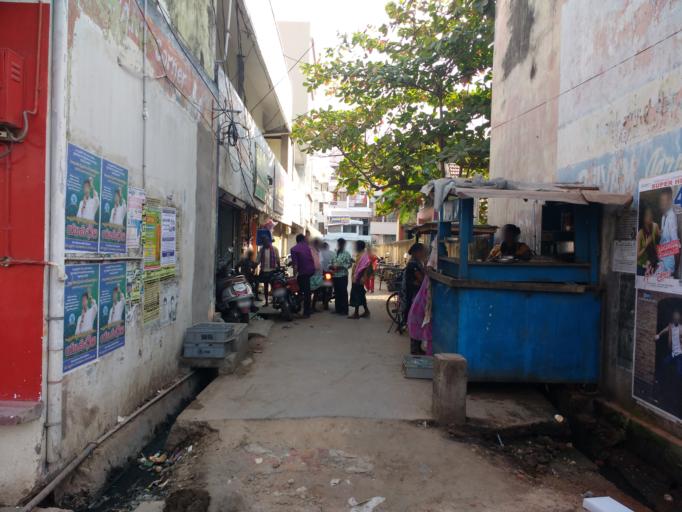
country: IN
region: Andhra Pradesh
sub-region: Srikakulam
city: Srikakulam
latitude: 18.2949
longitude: 83.8957
